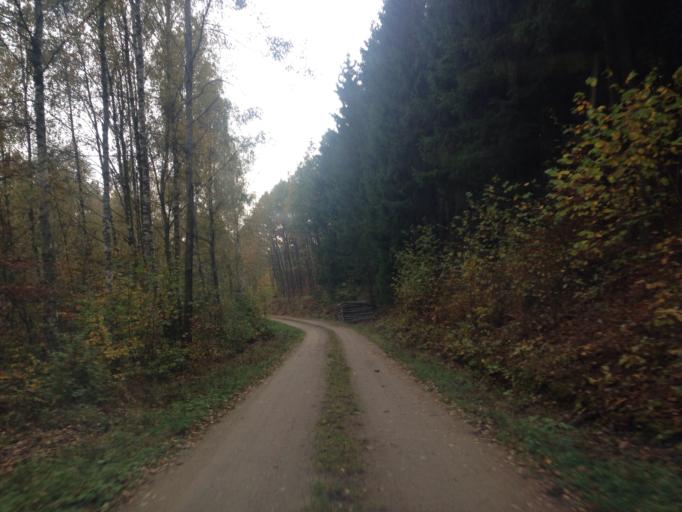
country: PL
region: Warmian-Masurian Voivodeship
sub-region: Powiat dzialdowski
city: Lidzbark
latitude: 53.2641
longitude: 19.7266
